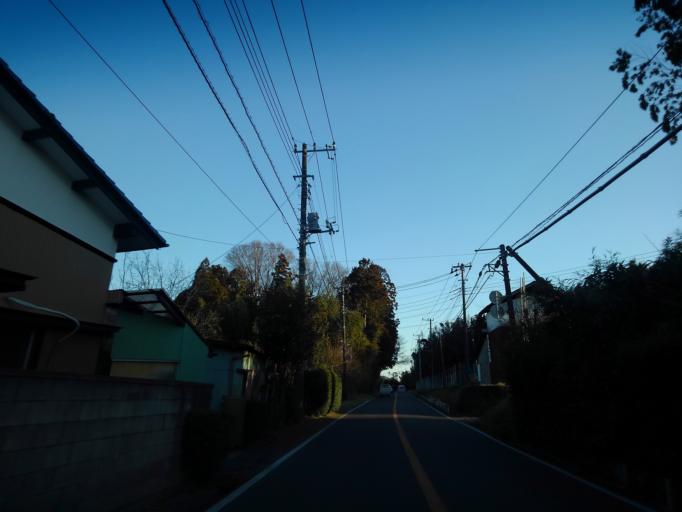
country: JP
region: Chiba
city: Kimitsu
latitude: 35.2979
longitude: 139.9790
